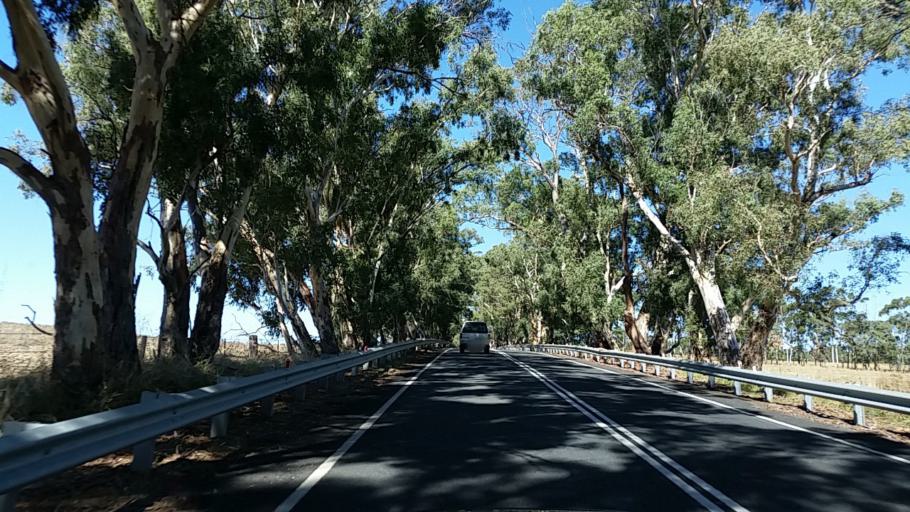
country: AU
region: South Australia
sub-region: Adelaide Hills
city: Birdwood
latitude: -34.7546
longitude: 138.9992
